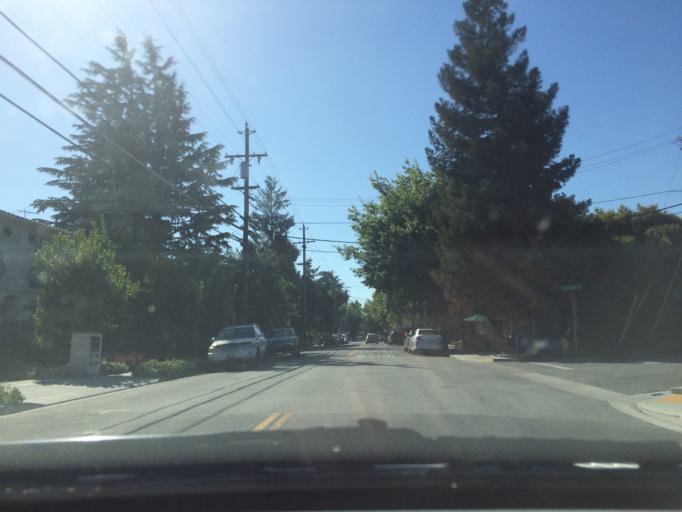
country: US
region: California
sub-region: San Mateo County
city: Menlo Park
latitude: 37.4480
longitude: -122.1838
